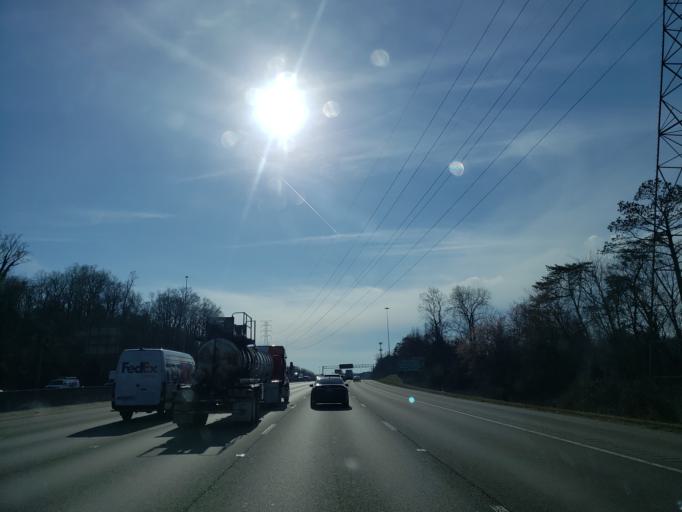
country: US
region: Tennessee
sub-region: Knox County
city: Knoxville
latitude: 35.9514
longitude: -83.9837
